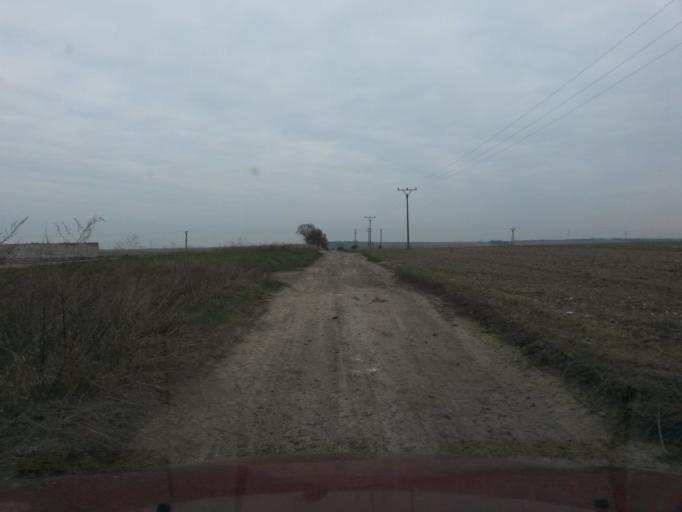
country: SK
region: Kosicky
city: Secovce
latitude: 48.6399
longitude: 21.5856
